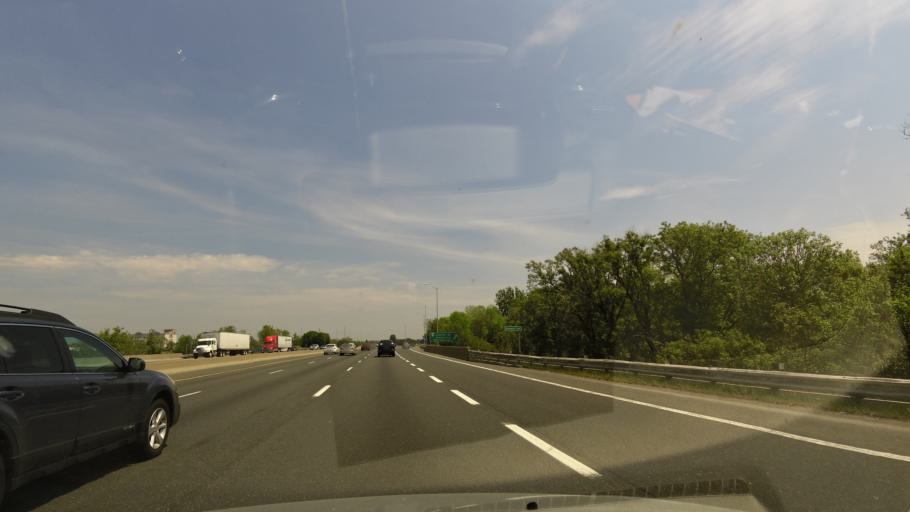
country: CA
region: Ontario
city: Oshawa
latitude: 43.8975
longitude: -78.6802
